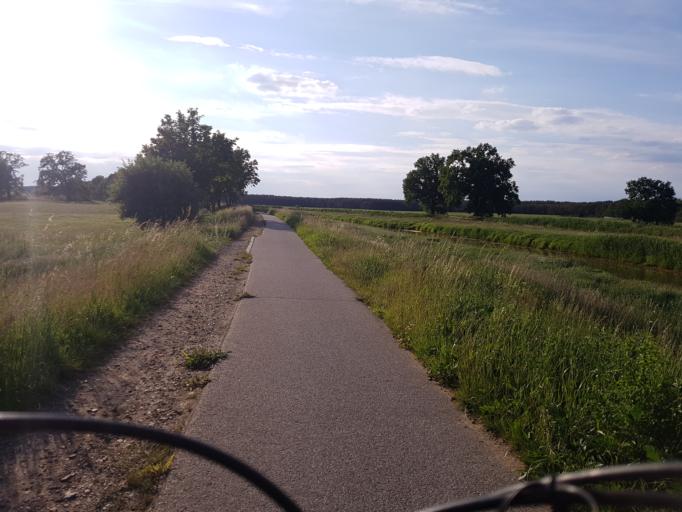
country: DE
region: Brandenburg
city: Elsterwerda
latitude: 51.4782
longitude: 13.4625
